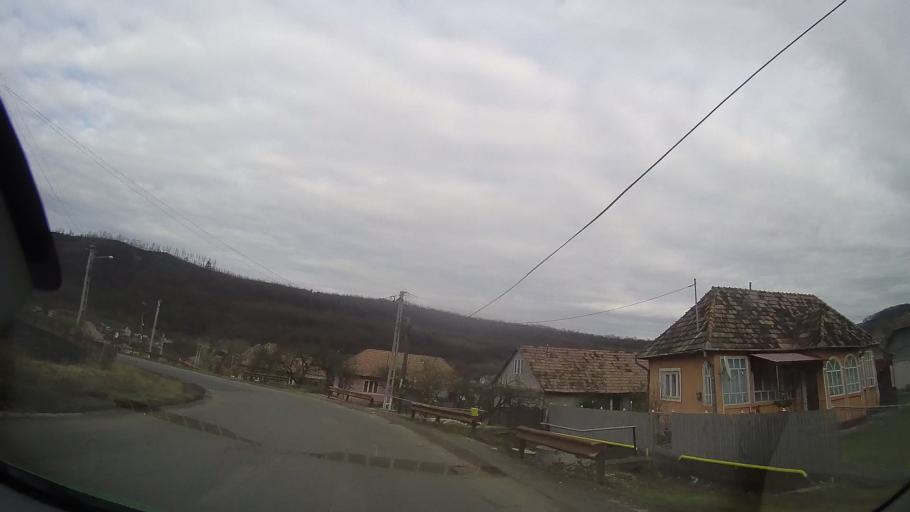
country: RO
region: Bistrita-Nasaud
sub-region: Comuna Silvasu de Campie
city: Silvasu de Campie
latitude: 46.7816
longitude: 24.2937
